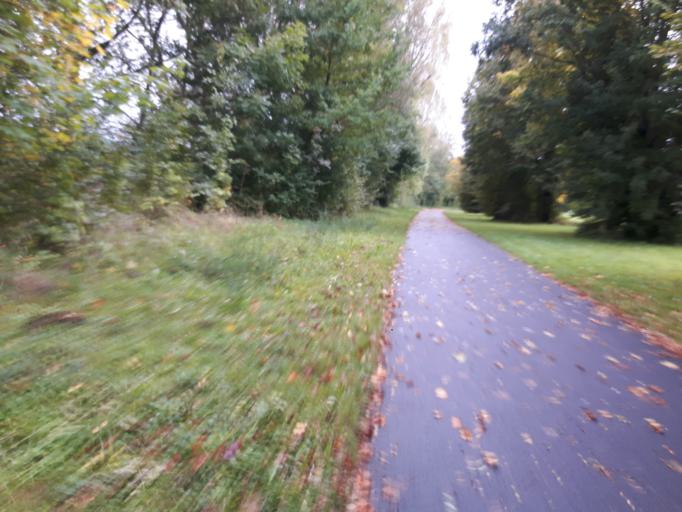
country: DE
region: Bavaria
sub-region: Regierungsbezirk Unterfranken
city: Thungersheim
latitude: 49.8844
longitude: 9.8330
